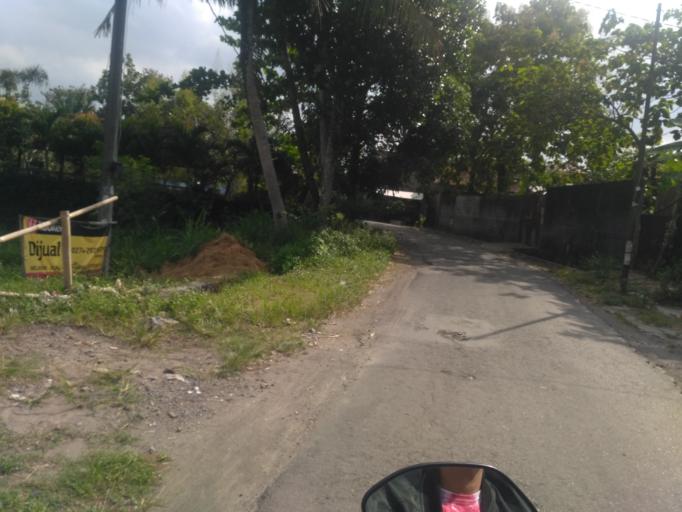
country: ID
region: Daerah Istimewa Yogyakarta
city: Yogyakarta
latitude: -7.7619
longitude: 110.3590
